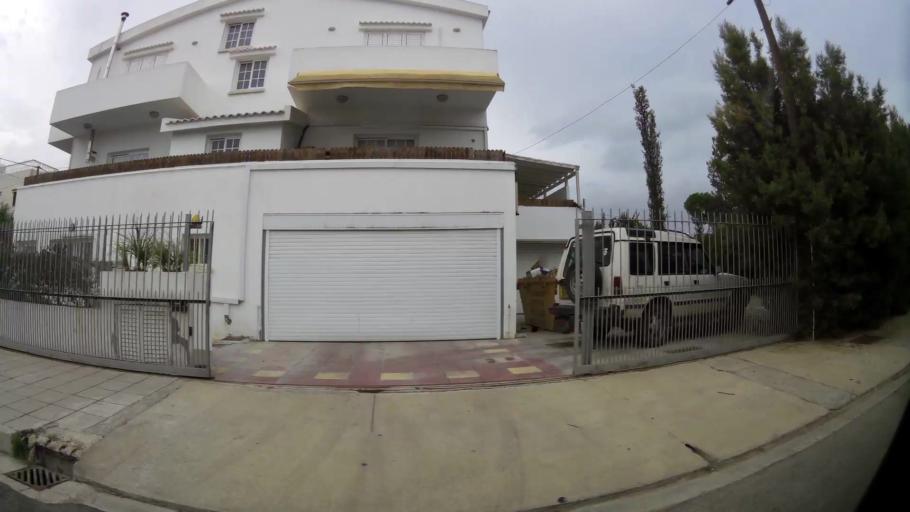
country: CY
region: Lefkosia
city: Geri
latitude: 35.0993
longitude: 33.3926
